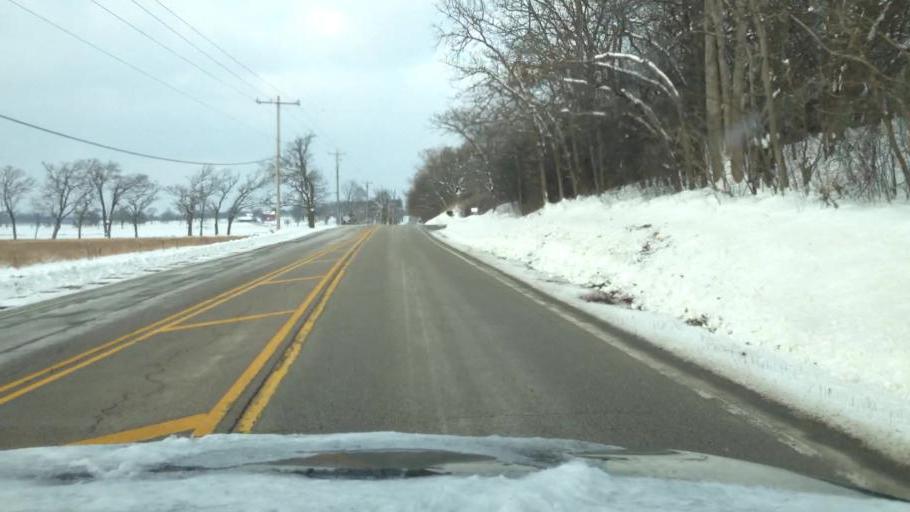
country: US
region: Wisconsin
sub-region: Waukesha County
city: North Prairie
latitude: 42.8910
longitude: -88.4169
